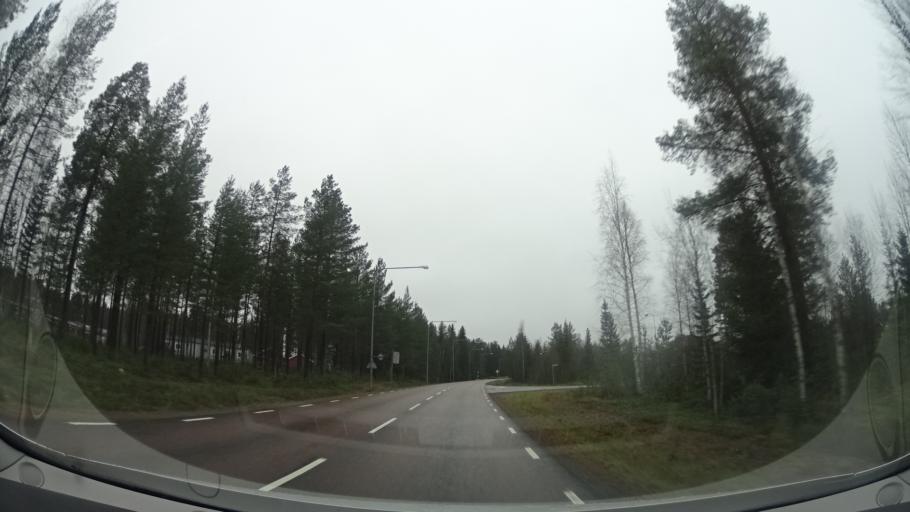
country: SE
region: Vaesterbotten
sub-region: Skelleftea Kommun
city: Skelleftea
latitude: 64.7555
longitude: 21.0259
